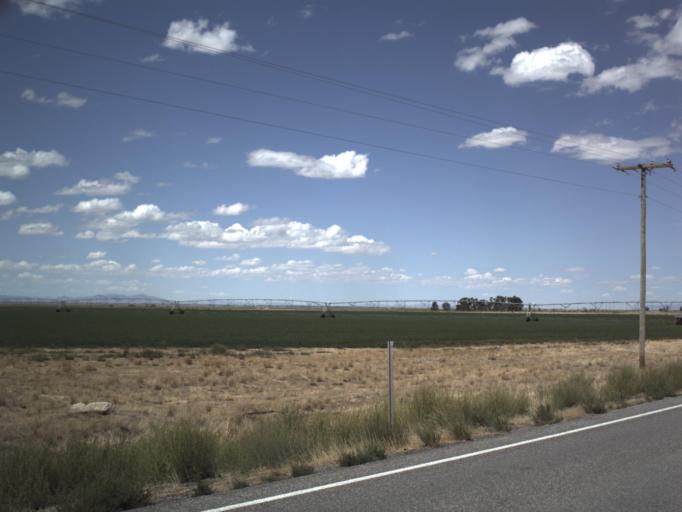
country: US
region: Utah
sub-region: Millard County
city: Delta
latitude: 39.1885
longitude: -112.4100
